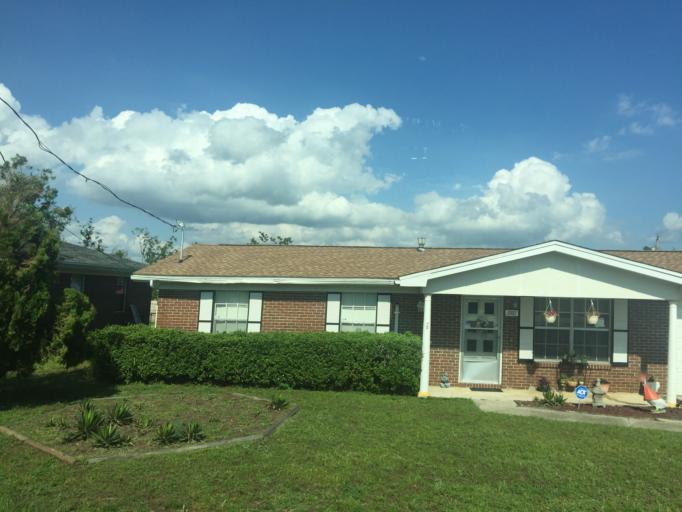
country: US
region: Florida
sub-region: Bay County
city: Springfield
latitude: 30.1669
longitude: -85.6036
